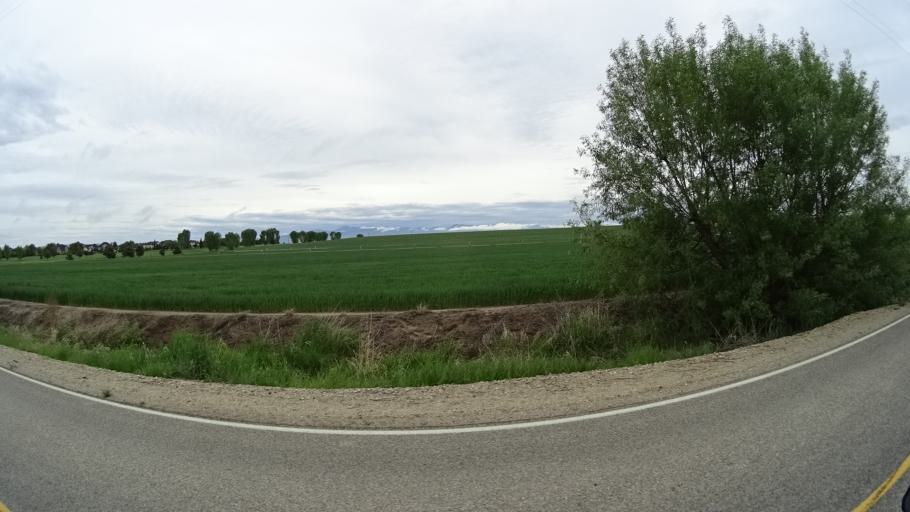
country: US
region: Idaho
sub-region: Ada County
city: Star
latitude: 43.7163
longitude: -116.4683
